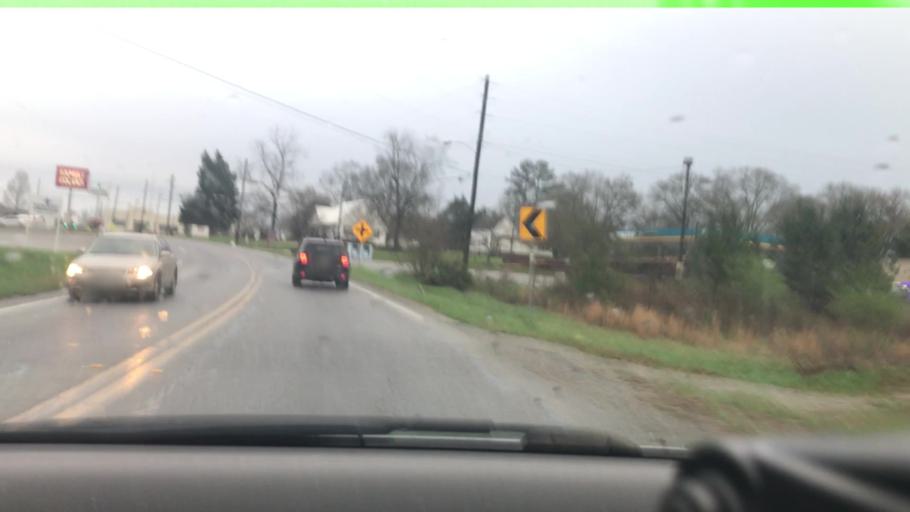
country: US
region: Georgia
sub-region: Oglethorpe County
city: Lexington
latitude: 33.8816
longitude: -83.1588
